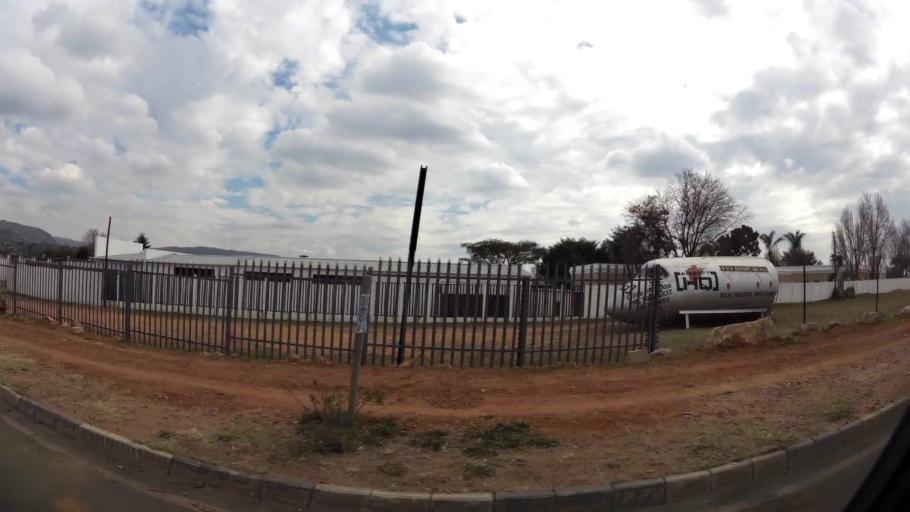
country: ZA
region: Gauteng
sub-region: West Rand District Municipality
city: Muldersdriseloop
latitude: -26.0842
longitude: 27.8740
